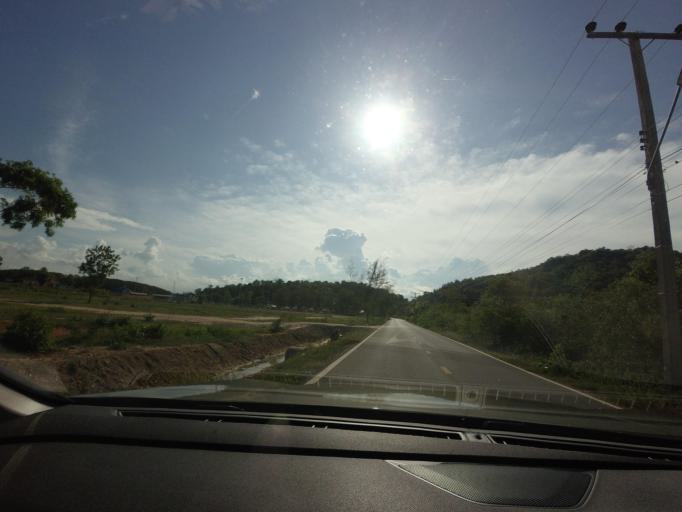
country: TH
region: Prachuap Khiri Khan
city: Pran Buri
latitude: 12.4094
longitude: 99.9814
